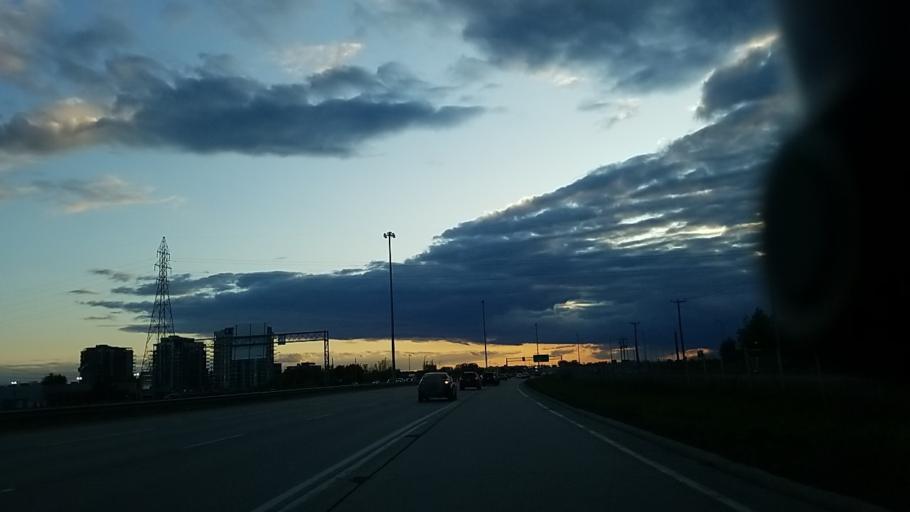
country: CA
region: Quebec
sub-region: Laval
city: Laval
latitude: 45.5700
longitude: -73.7610
